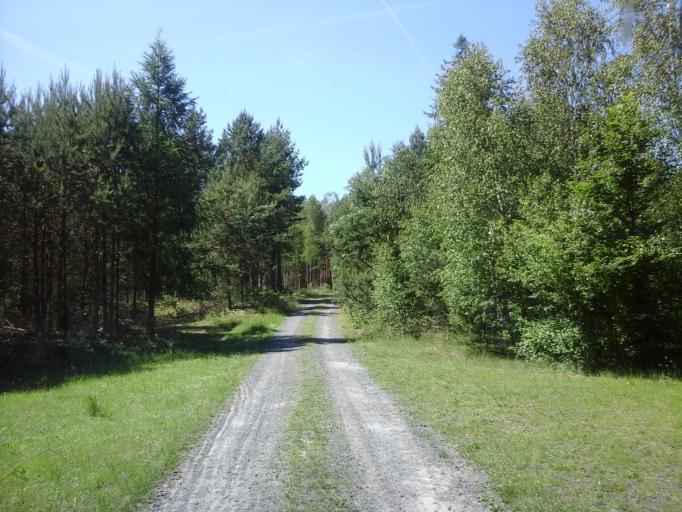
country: PL
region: West Pomeranian Voivodeship
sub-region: Powiat drawski
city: Kalisz Pomorski
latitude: 53.2151
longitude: 15.9880
